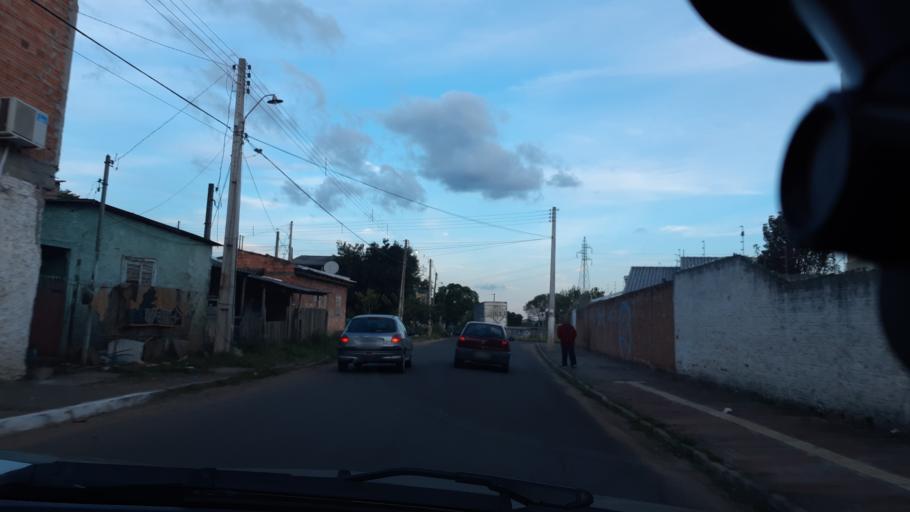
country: BR
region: Rio Grande do Sul
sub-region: Sapucaia Do Sul
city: Sapucaia
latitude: -29.8402
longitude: -51.1547
